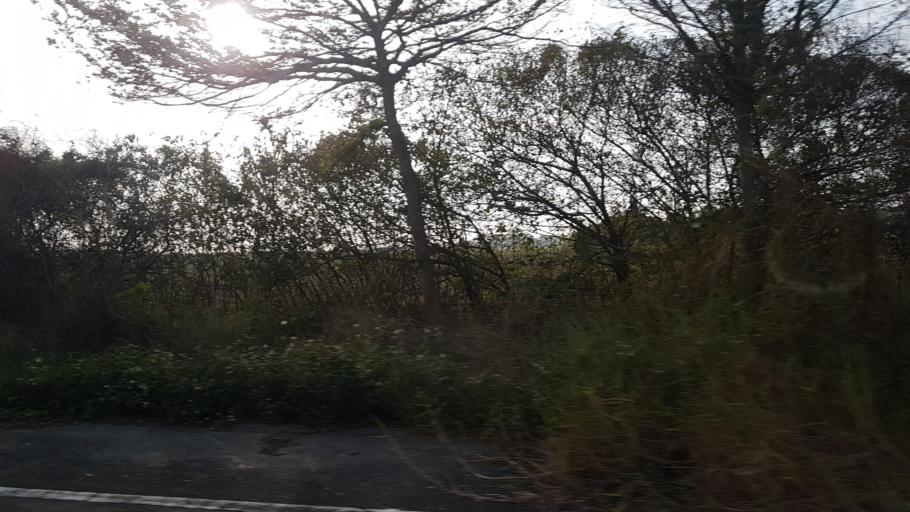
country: TW
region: Taiwan
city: Xinying
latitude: 23.3489
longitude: 120.3742
